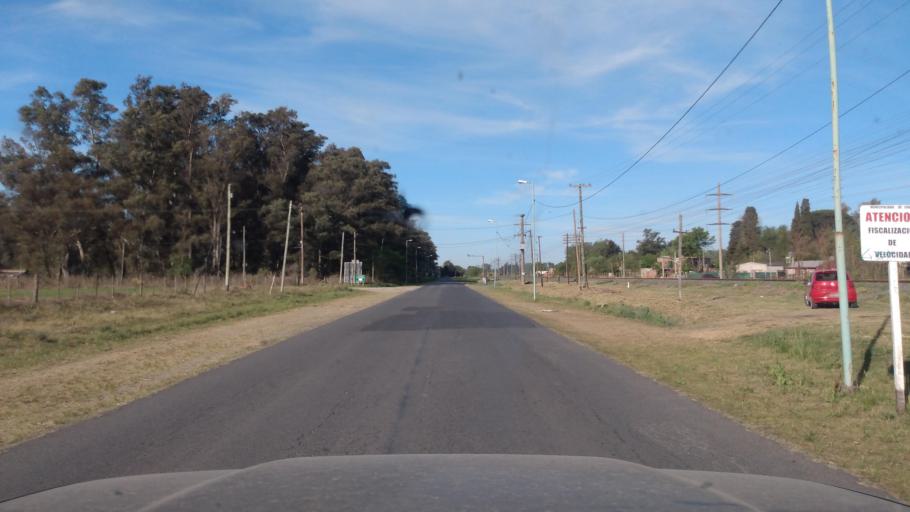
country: AR
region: Buenos Aires
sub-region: Partido de Lujan
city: Lujan
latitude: -34.5881
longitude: -59.1366
